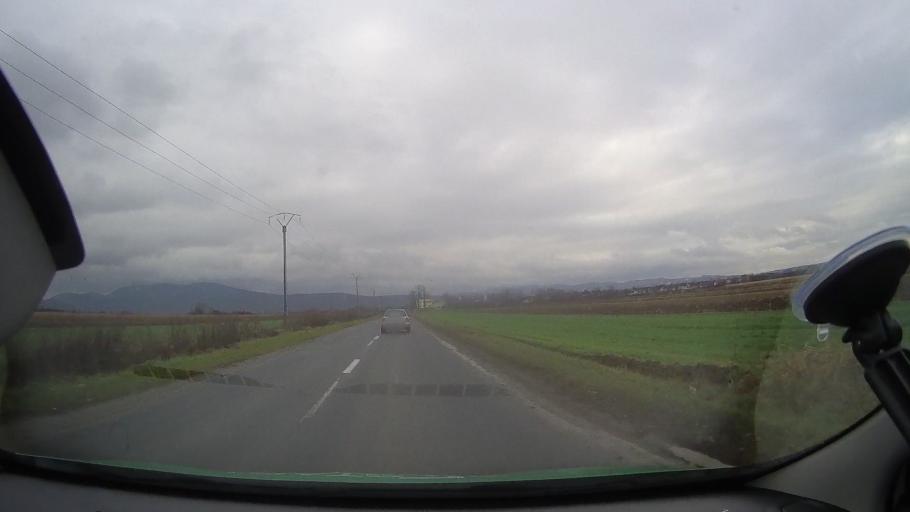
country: RO
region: Arad
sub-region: Comuna Buteni
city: Buteni
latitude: 46.3393
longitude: 22.1276
